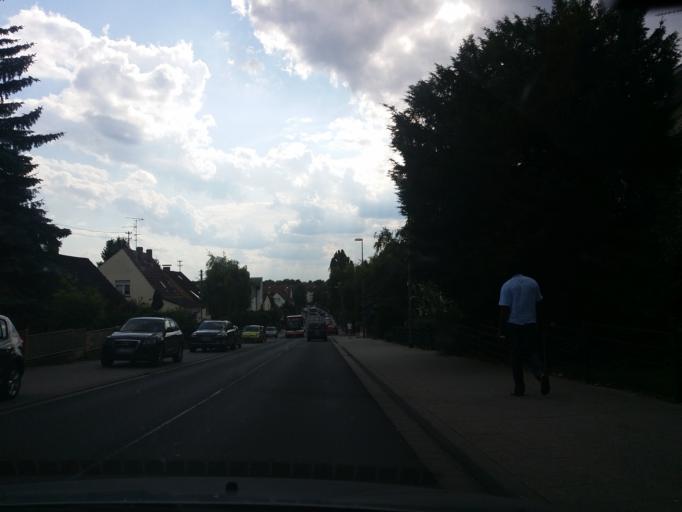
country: DE
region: Hesse
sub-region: Regierungsbezirk Darmstadt
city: Wiesbaden
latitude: 50.0876
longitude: 8.2889
